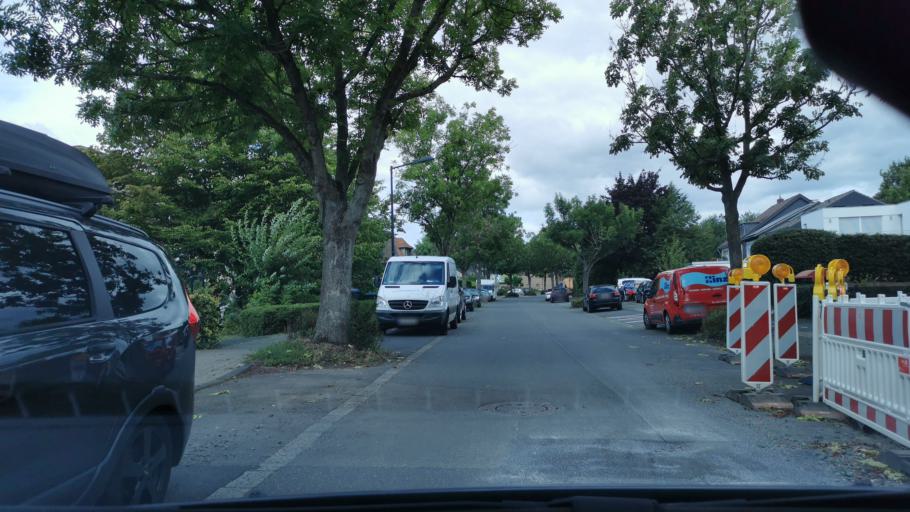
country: DE
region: North Rhine-Westphalia
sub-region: Regierungsbezirk Koln
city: Hurth
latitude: 50.9001
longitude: 6.8912
